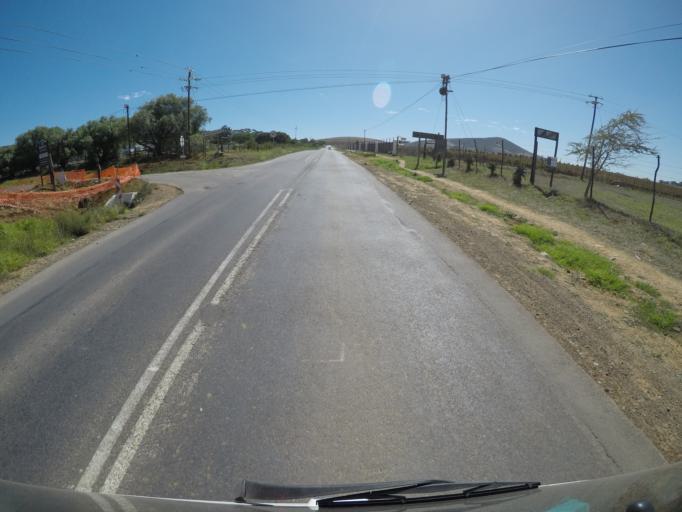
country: ZA
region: Western Cape
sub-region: City of Cape Town
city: Kraaifontein
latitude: -33.8095
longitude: 18.6253
